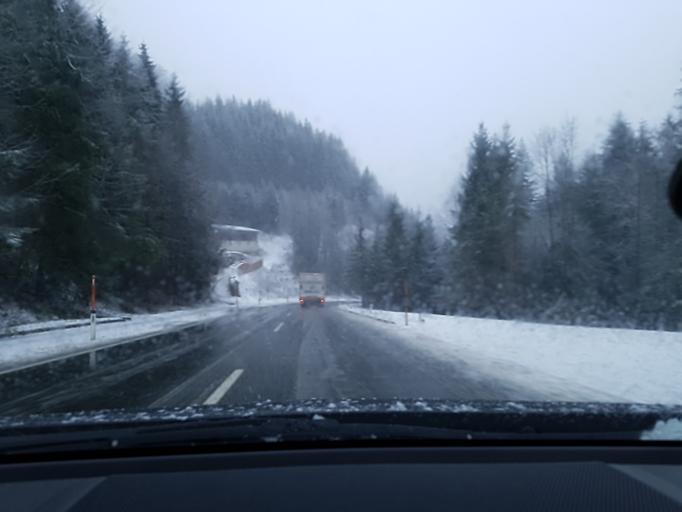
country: AT
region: Salzburg
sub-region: Politischer Bezirk Hallein
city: Scheffau am Tennengebirge
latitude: 47.5798
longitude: 13.2700
